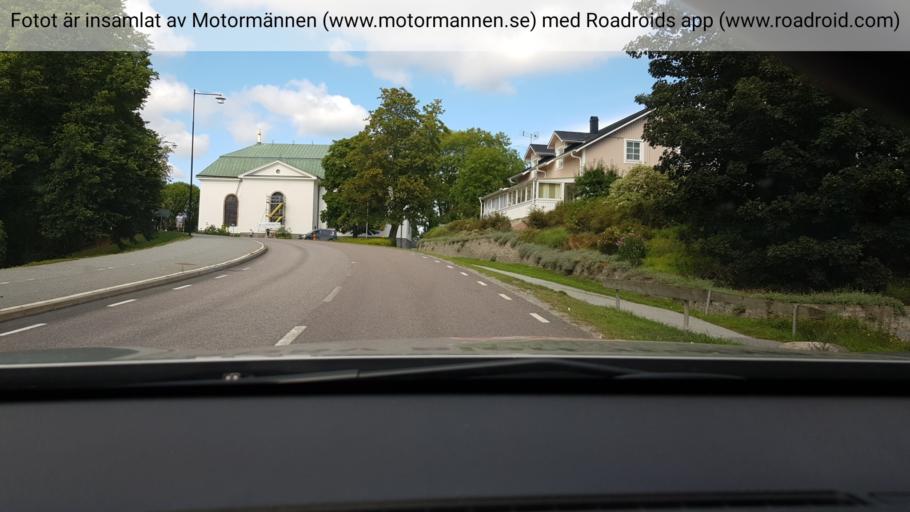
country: SE
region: Stockholm
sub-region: Vaxholms Kommun
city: Vaxholm
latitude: 59.4024
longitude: 18.3484
